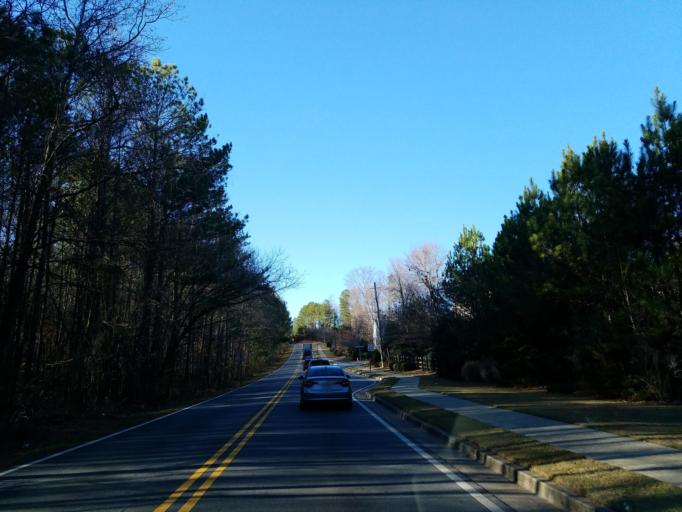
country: US
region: Georgia
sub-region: Cobb County
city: Mableton
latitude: 33.7754
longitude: -84.5552
